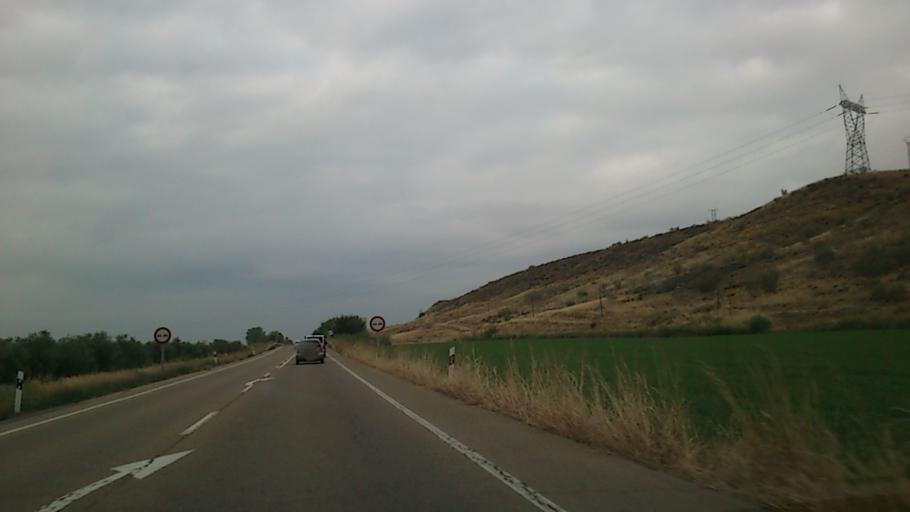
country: ES
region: Aragon
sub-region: Provincia de Zaragoza
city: San Mateo de Gallego
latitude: 41.8212
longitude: -0.8027
